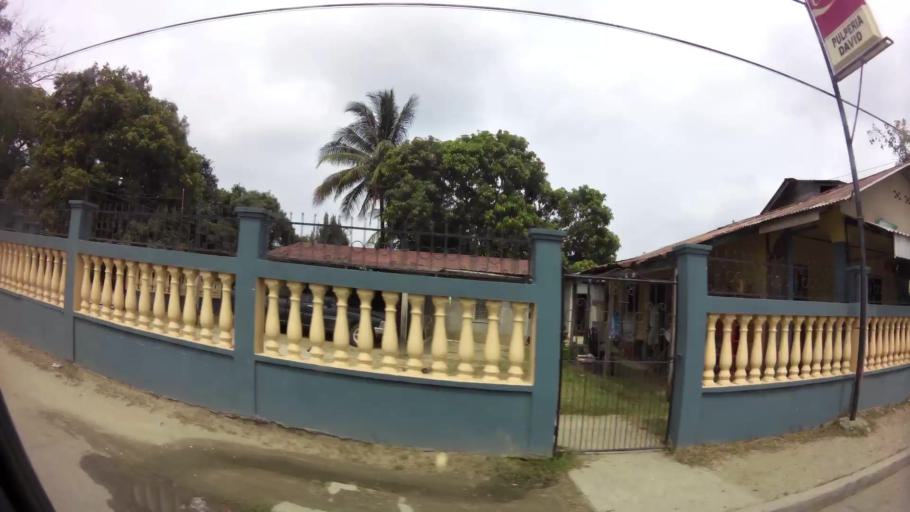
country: HN
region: Atlantida
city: Tela
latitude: 15.7699
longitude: -87.4817
